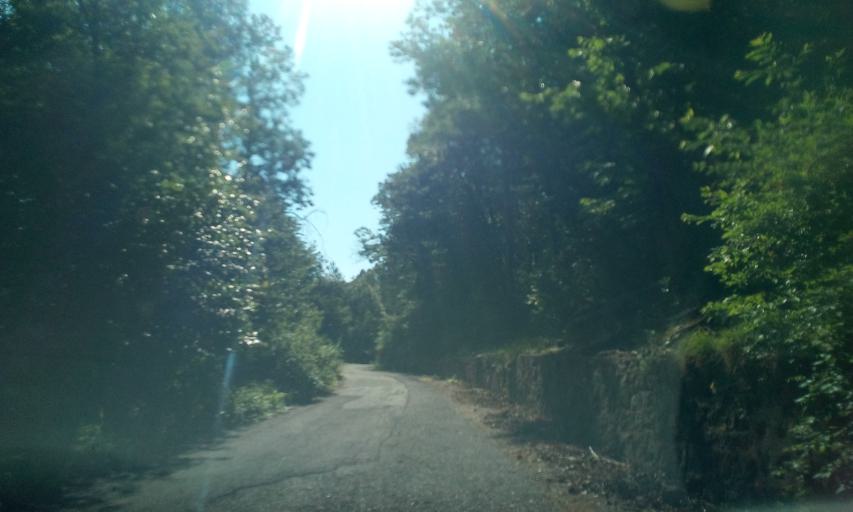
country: IT
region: Aosta Valley
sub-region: Valle d'Aosta
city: Saint-Vincent
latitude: 45.7369
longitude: 7.6373
